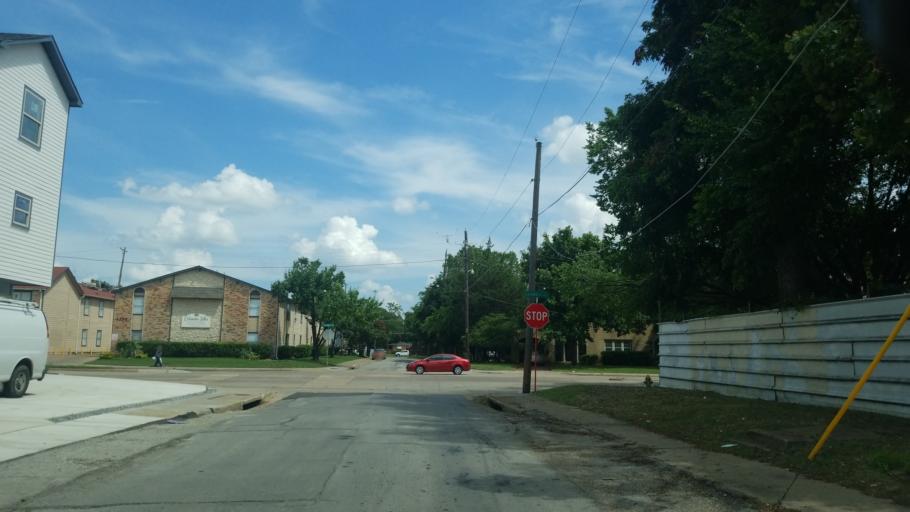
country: US
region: Texas
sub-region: Dallas County
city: Dallas
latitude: 32.7938
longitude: -96.7660
